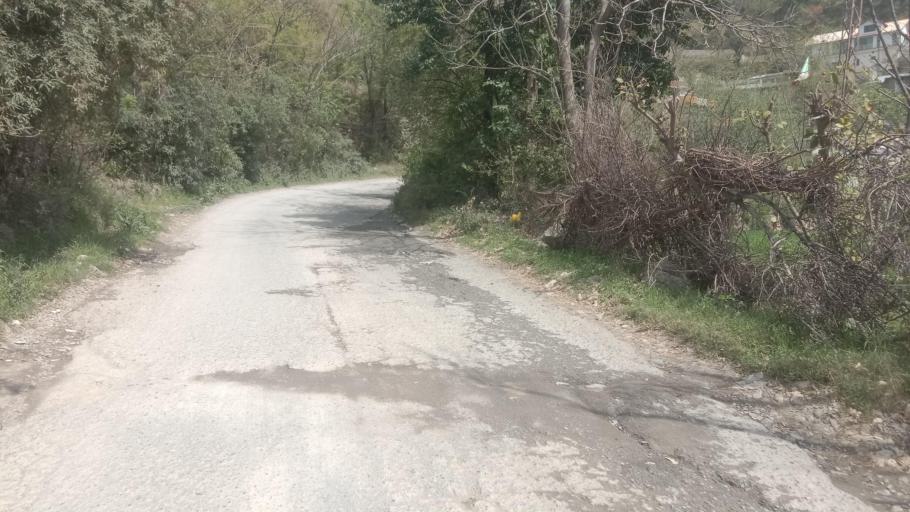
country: PK
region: Khyber Pakhtunkhwa
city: Abbottabad
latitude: 34.1680
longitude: 73.2810
